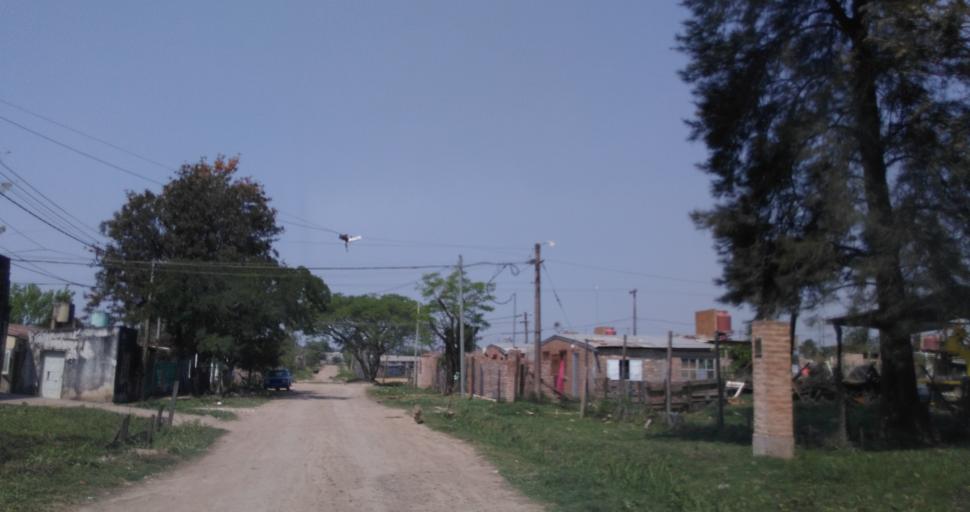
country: AR
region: Chaco
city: Fontana
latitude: -27.4223
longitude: -59.0254
